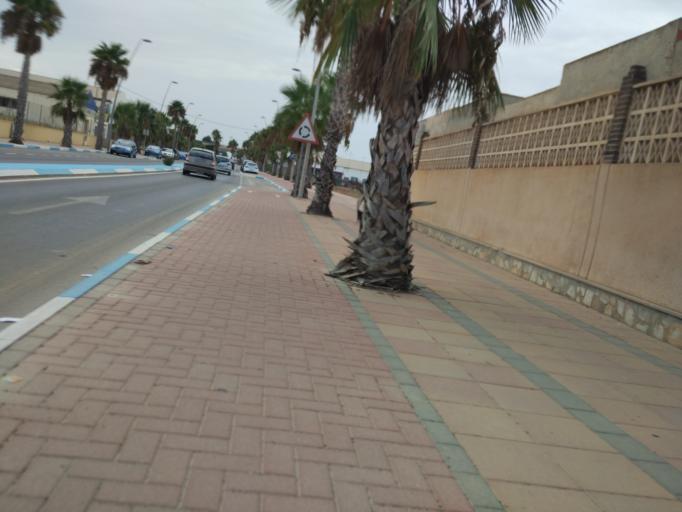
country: ES
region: Murcia
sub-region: Murcia
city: Los Alcazares
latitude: 37.7388
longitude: -0.8683
